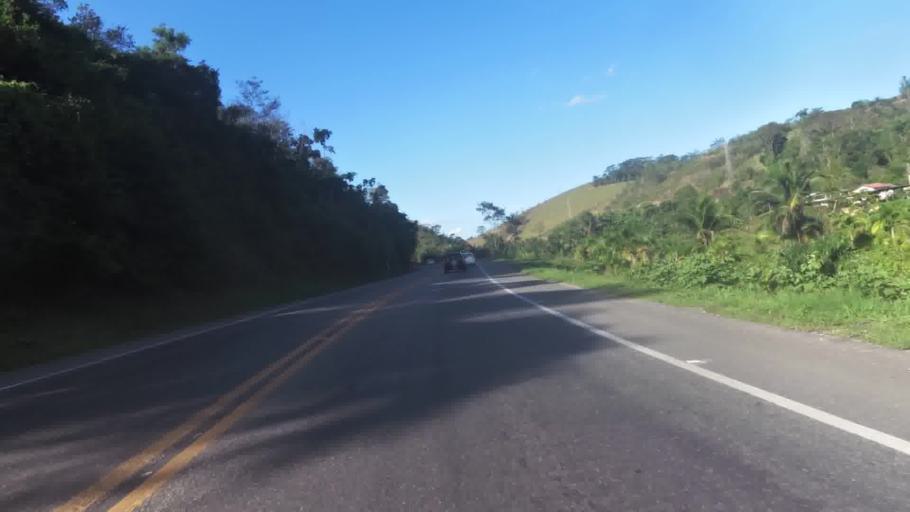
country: BR
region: Espirito Santo
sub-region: Iconha
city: Iconha
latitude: -20.8294
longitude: -40.8580
